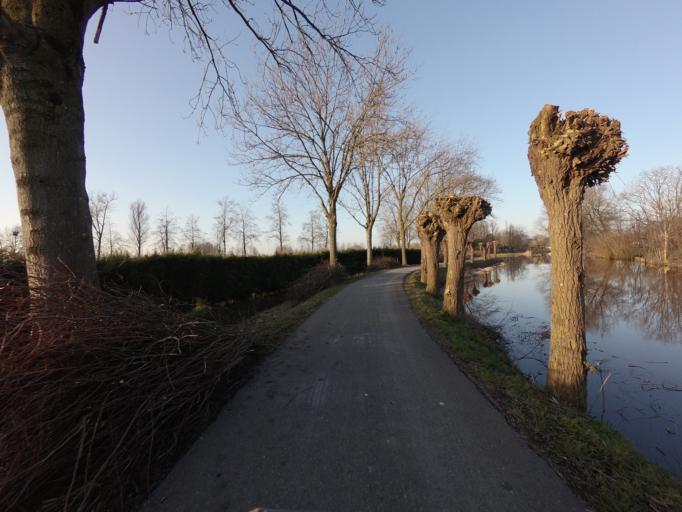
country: NL
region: South Holland
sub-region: Gemeente Giessenlanden
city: Giessenburg
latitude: 51.8961
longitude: 4.9306
